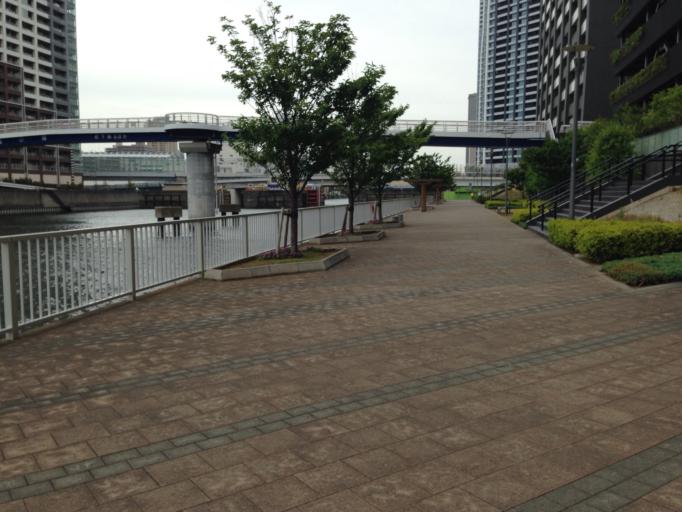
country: JP
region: Tokyo
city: Tokyo
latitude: 35.6531
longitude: 139.7744
